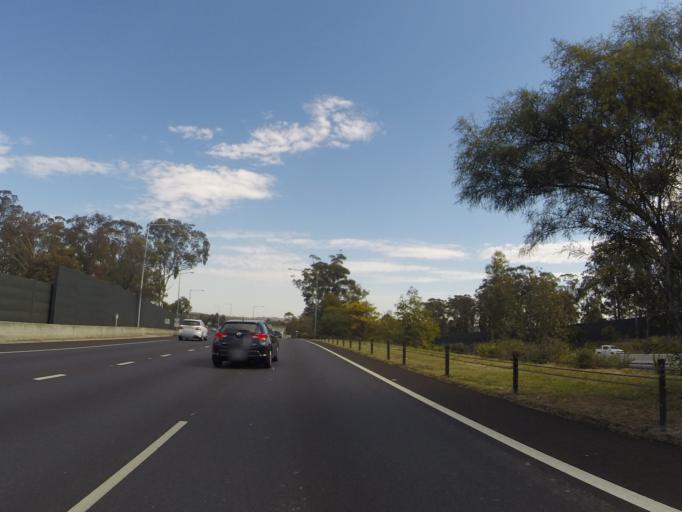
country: AU
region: New South Wales
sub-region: Campbelltown Municipality
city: Glenfield
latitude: -33.9498
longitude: 150.8861
